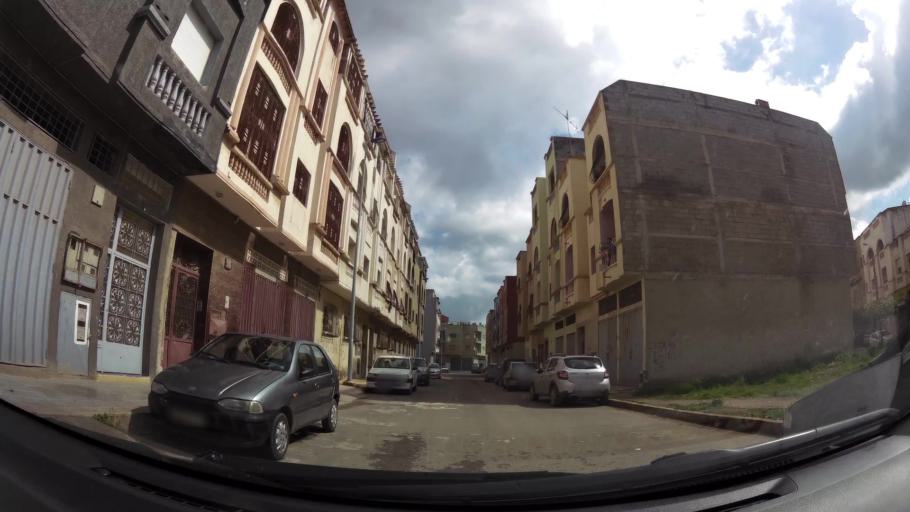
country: MA
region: Chaouia-Ouardigha
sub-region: Settat Province
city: Berrechid
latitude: 33.2763
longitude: -7.5891
